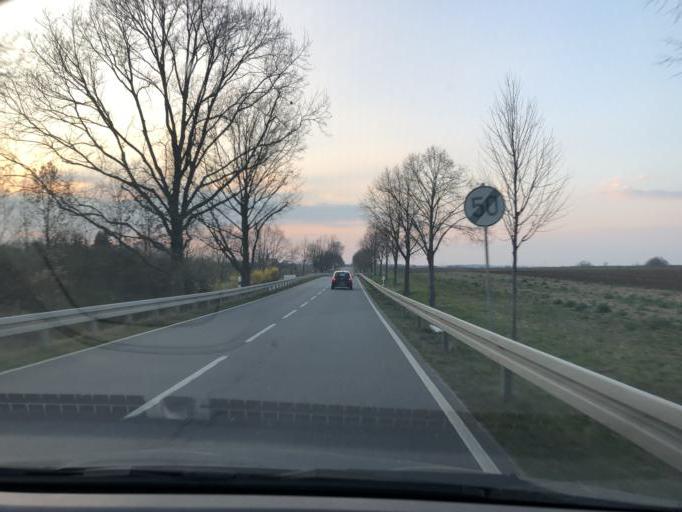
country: DE
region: Saxony
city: Panschwitz-Kuckau
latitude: 51.2287
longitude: 14.2126
